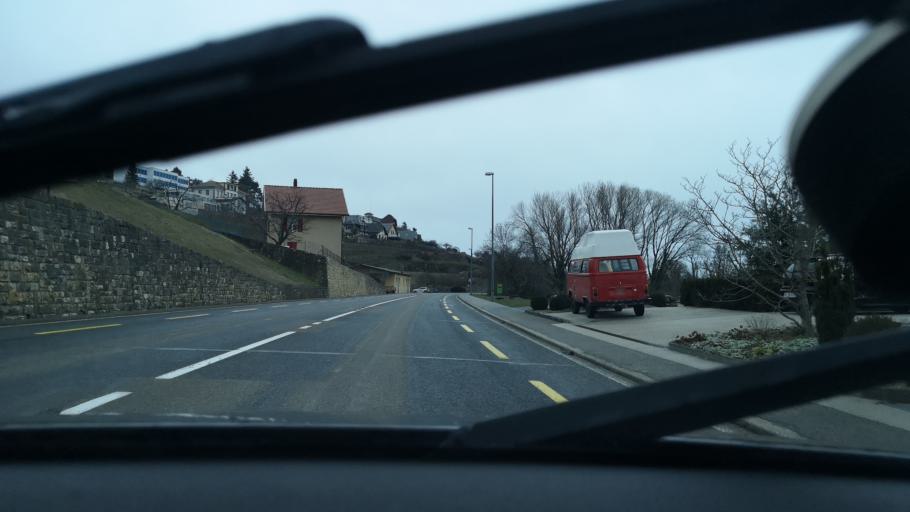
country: CH
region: Neuchatel
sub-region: Boudry District
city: Saint-Aubin-Sauges
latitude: 46.8895
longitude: 6.7676
